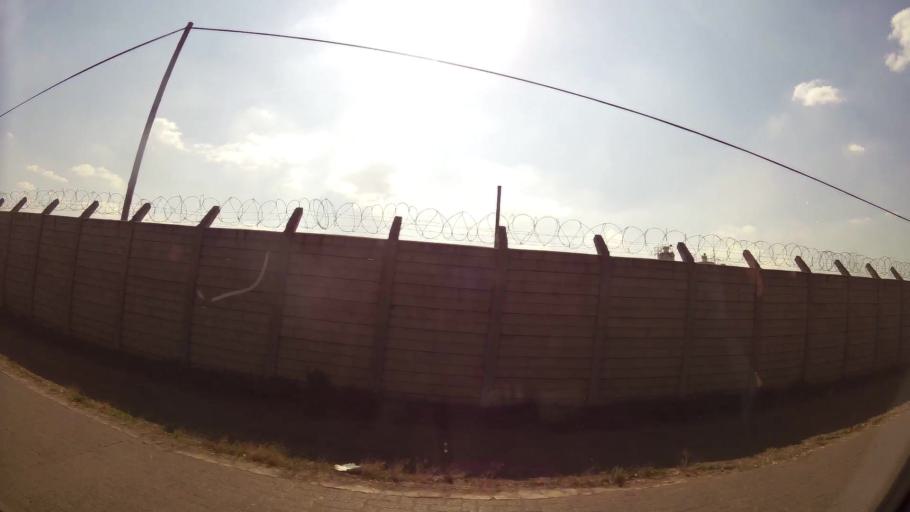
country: ZA
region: Gauteng
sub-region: Ekurhuleni Metropolitan Municipality
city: Boksburg
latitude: -26.2087
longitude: 28.2815
